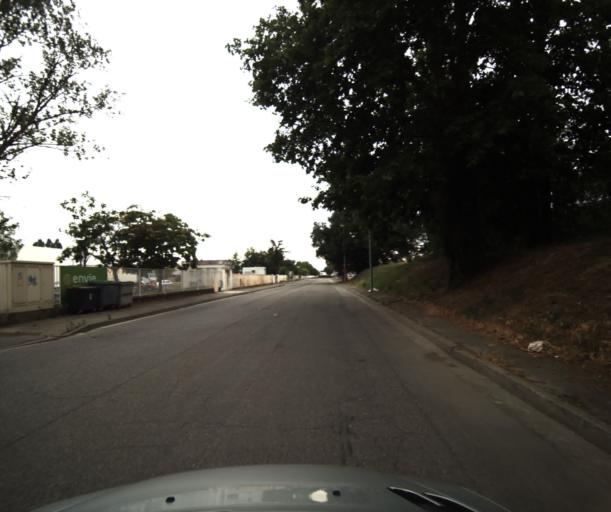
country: FR
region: Midi-Pyrenees
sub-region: Departement de la Haute-Garonne
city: Pinsaguel
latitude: 43.5284
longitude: 1.3819
